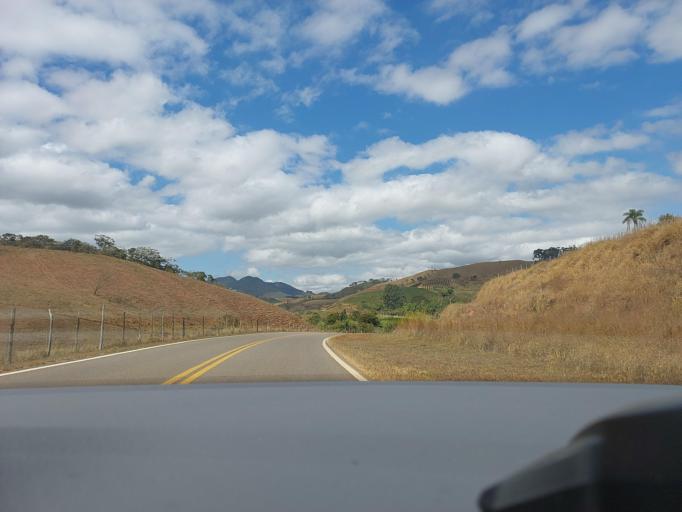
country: BR
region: Minas Gerais
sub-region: Visconde Do Rio Branco
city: Visconde do Rio Branco
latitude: -20.9247
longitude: -42.6362
